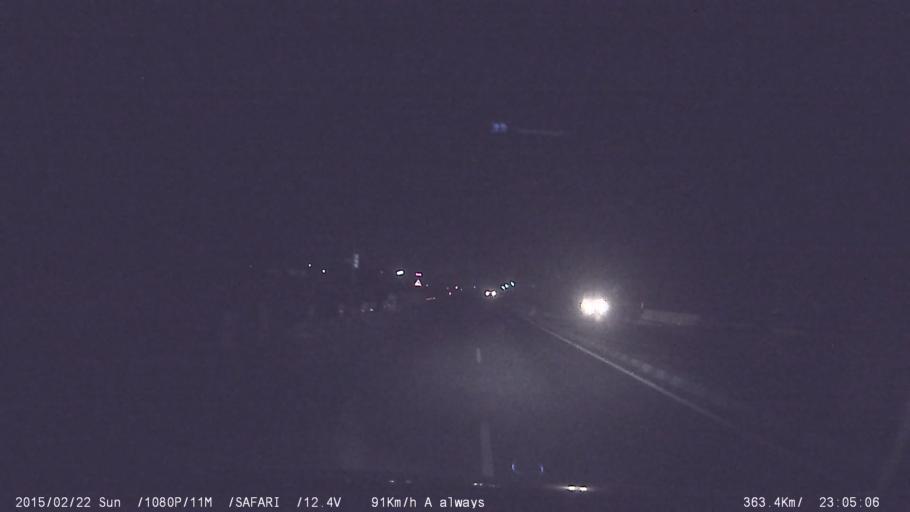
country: IN
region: Tamil Nadu
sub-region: Namakkal
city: Rasipuram
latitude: 11.4109
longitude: 78.1588
